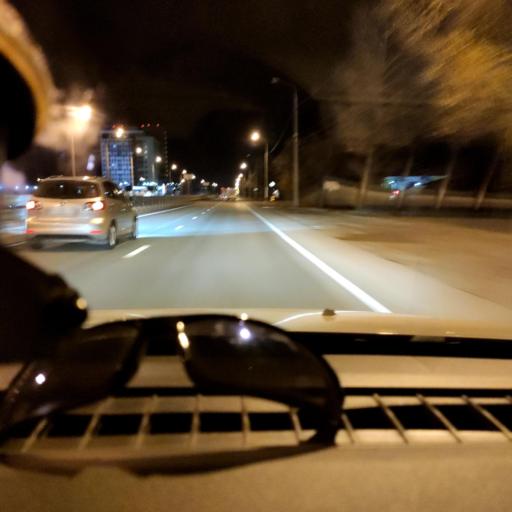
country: RU
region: Samara
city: Samara
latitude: 53.1141
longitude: 50.1662
